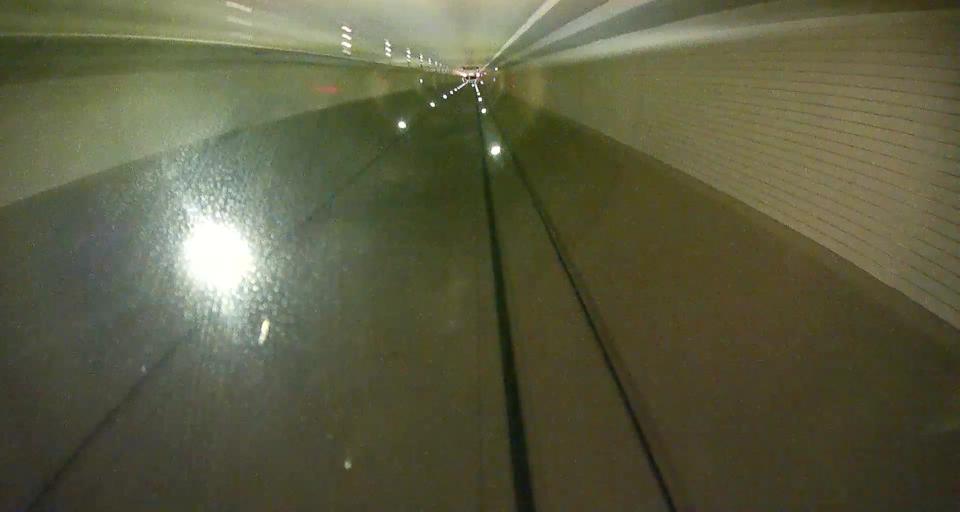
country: JP
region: Iwate
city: Miyako
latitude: 39.9308
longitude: 141.8597
